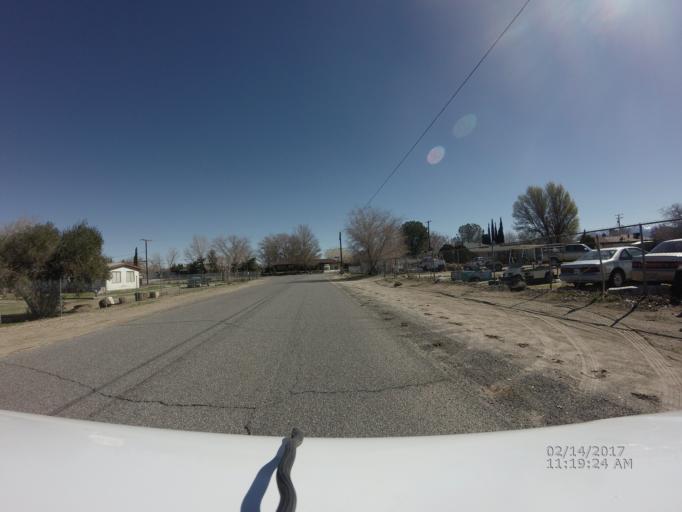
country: US
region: California
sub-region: Los Angeles County
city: Littlerock
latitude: 34.5633
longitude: -117.9615
